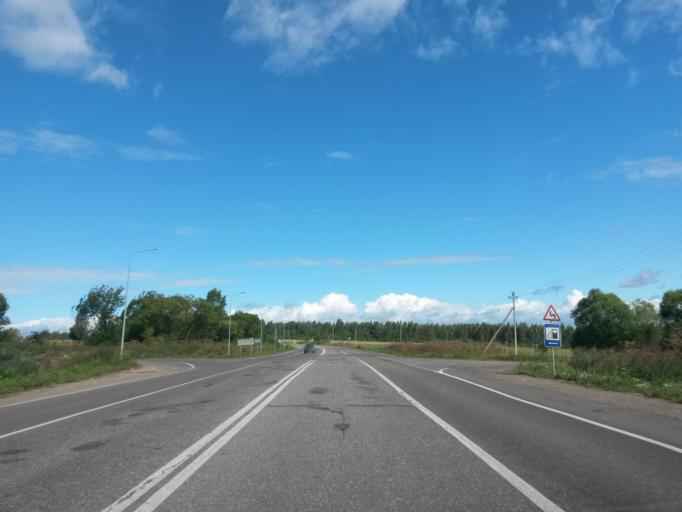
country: RU
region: Jaroslavl
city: Yaroslavl
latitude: 57.5532
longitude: 39.8614
